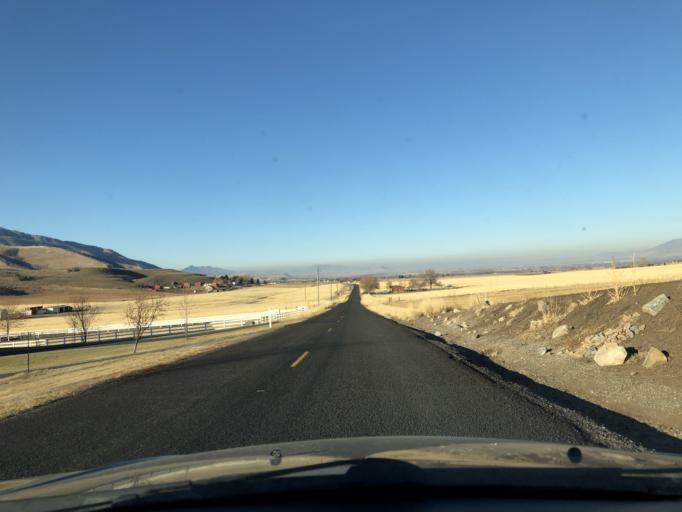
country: US
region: Utah
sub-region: Cache County
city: Wellsville
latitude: 41.5852
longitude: -111.9258
